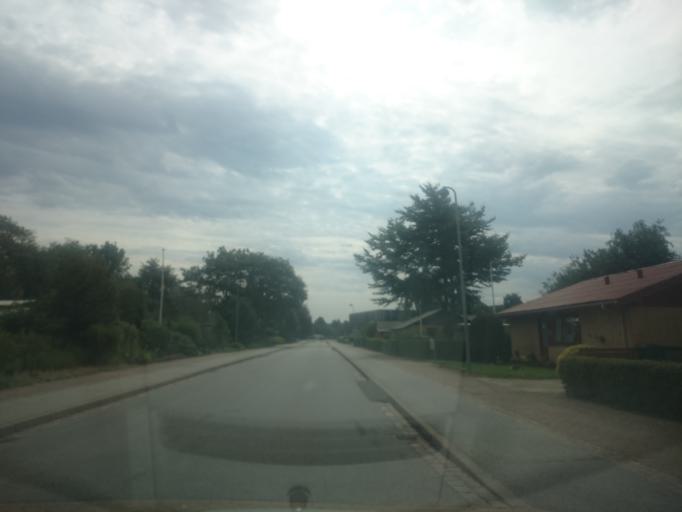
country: DK
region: South Denmark
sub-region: Billund Kommune
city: Billund
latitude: 55.7350
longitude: 9.1148
